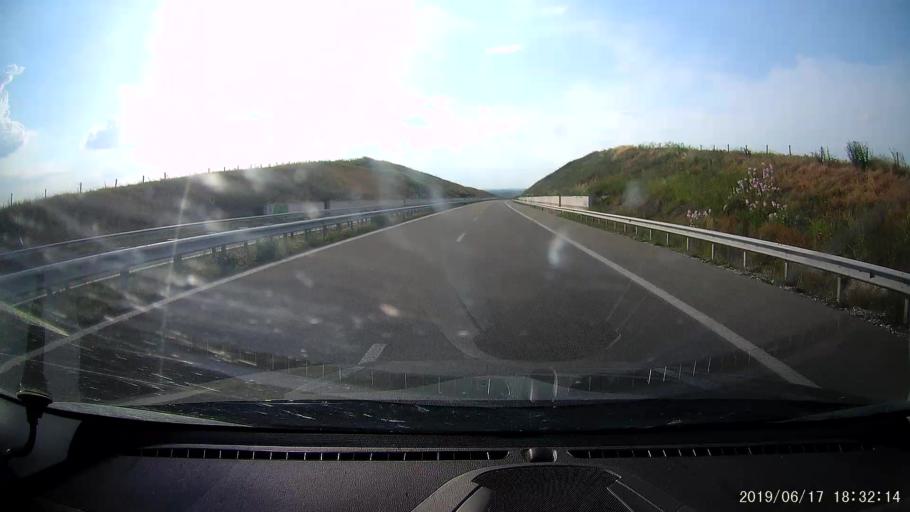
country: BG
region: Khaskovo
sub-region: Obshtina Dimitrovgrad
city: Dimitrovgrad
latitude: 42.0567
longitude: 25.4837
